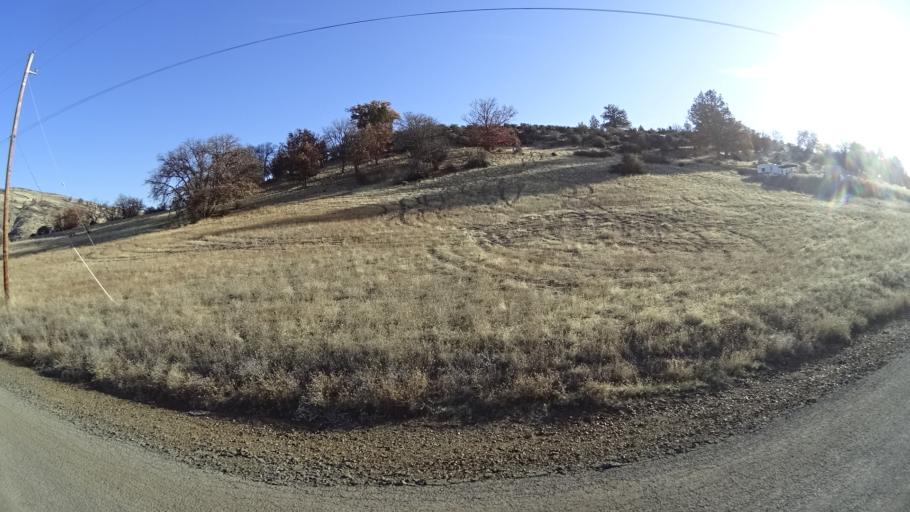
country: US
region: California
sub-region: Siskiyou County
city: Montague
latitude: 41.8951
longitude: -122.4945
